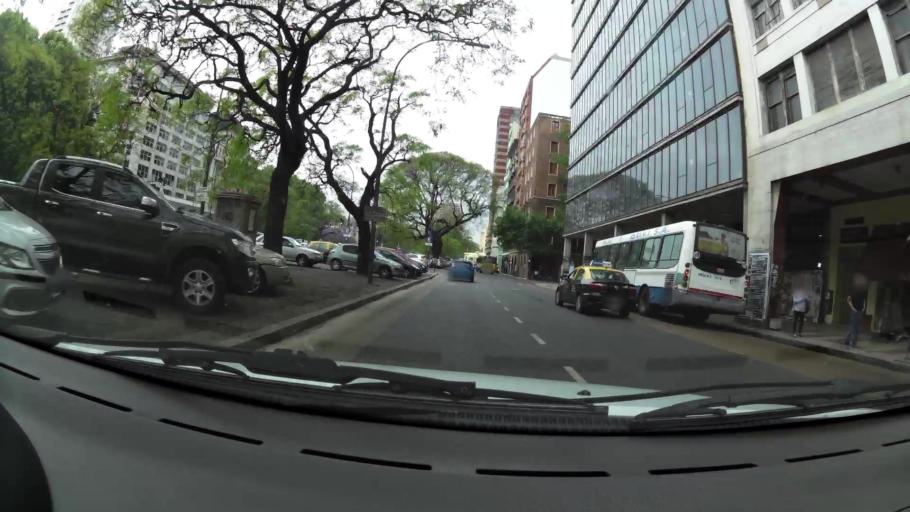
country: AR
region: Buenos Aires F.D.
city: Buenos Aires
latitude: -34.6154
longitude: -58.3694
